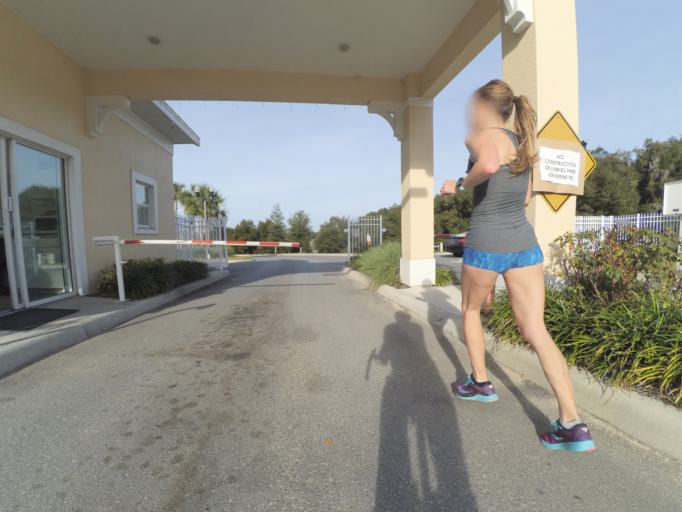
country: US
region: Florida
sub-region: Lake County
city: Umatilla
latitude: 28.9619
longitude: -81.6512
